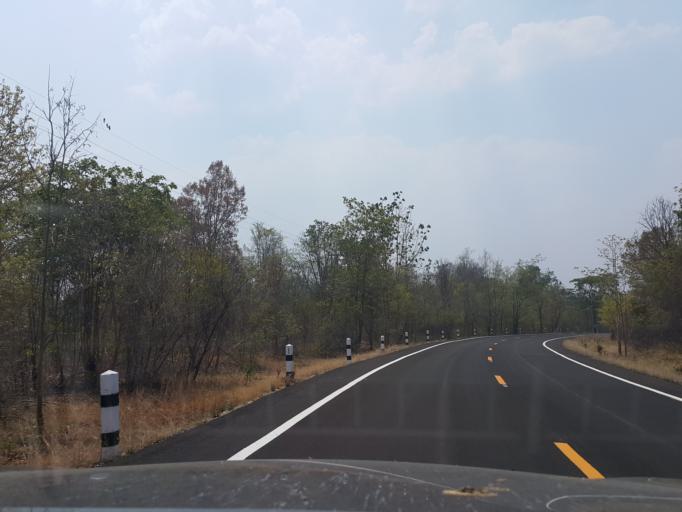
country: TH
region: Lampang
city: Mae Phrik
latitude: 17.4801
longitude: 99.1103
